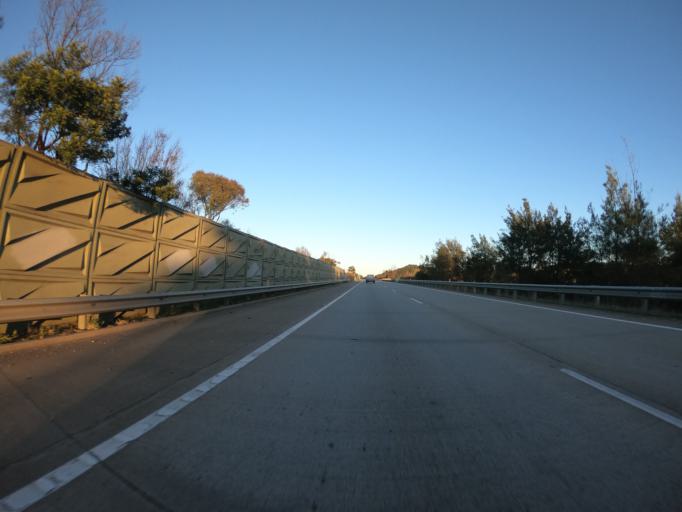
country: AU
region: New South Wales
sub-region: Goulburn Mulwaree
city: Goulburn
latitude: -34.7760
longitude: 149.7093
